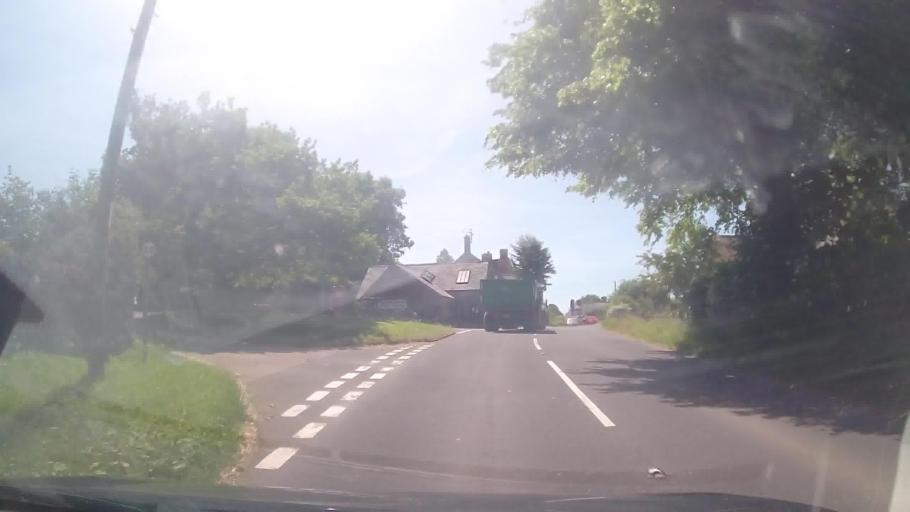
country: GB
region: England
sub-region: Herefordshire
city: Pencoyd
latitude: 51.9150
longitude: -2.7352
